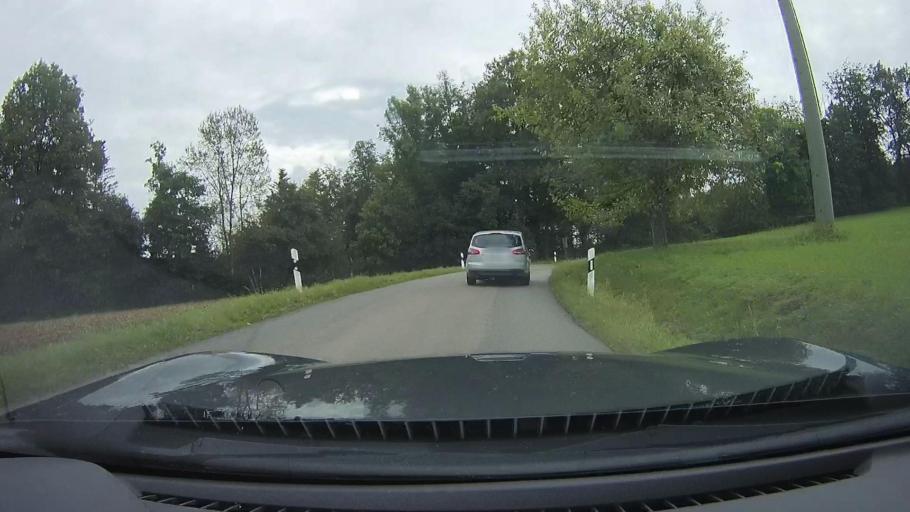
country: DE
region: Baden-Wuerttemberg
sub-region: Regierungsbezirk Stuttgart
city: Murrhardt
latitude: 49.0149
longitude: 9.5662
